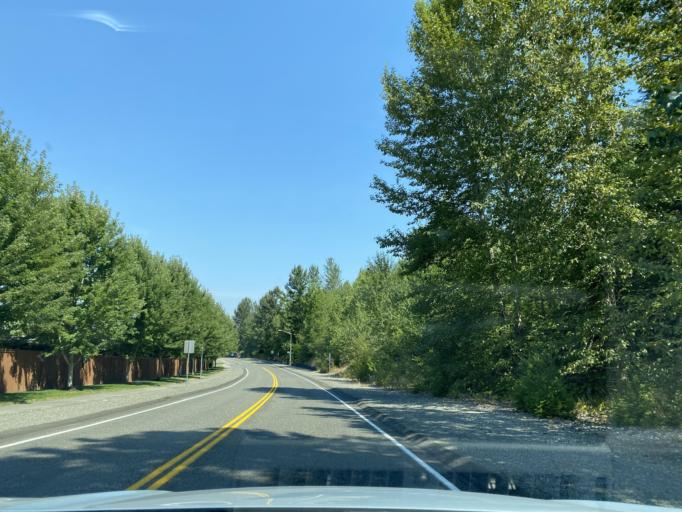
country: US
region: Washington
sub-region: Pierce County
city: Bonney Lake
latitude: 47.1642
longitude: -122.1923
